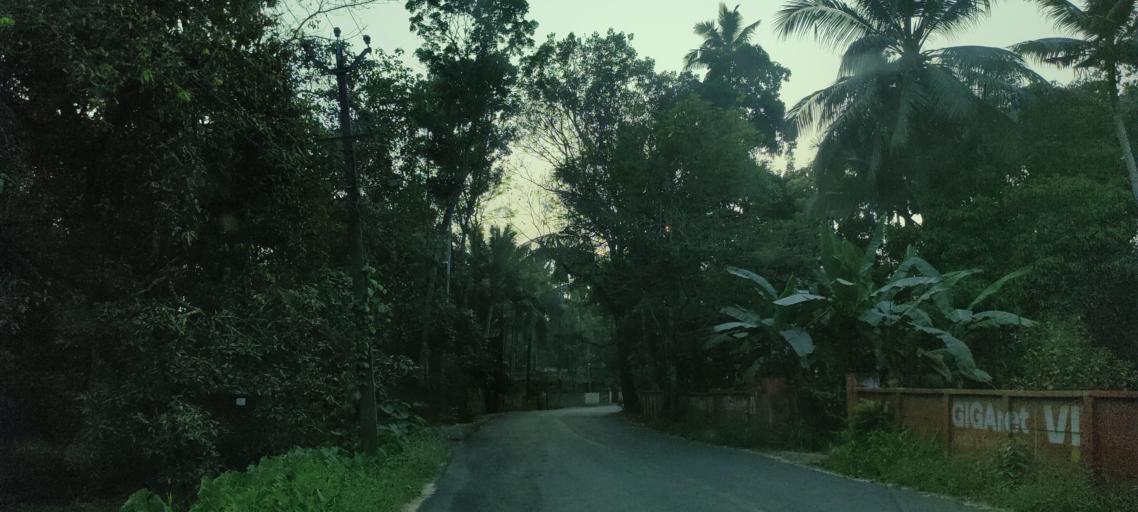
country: IN
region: Kerala
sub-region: Kottayam
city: Vaikam
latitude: 9.6876
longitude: 76.4260
